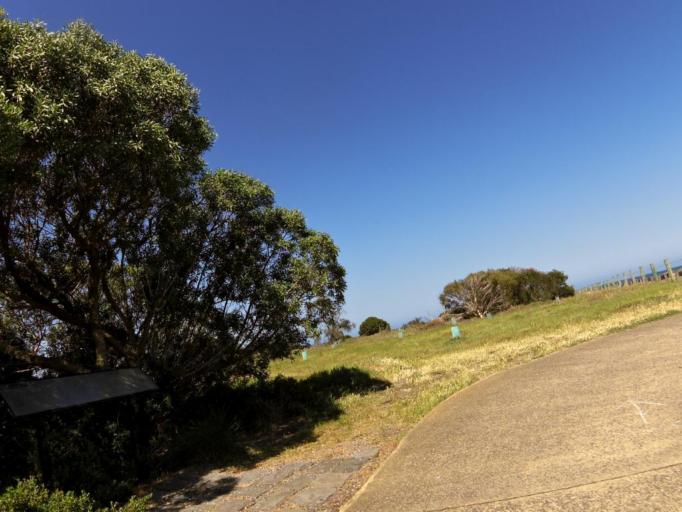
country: AU
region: Victoria
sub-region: Hobsons Bay
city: Seaholme
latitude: -37.8623
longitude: 144.8554
